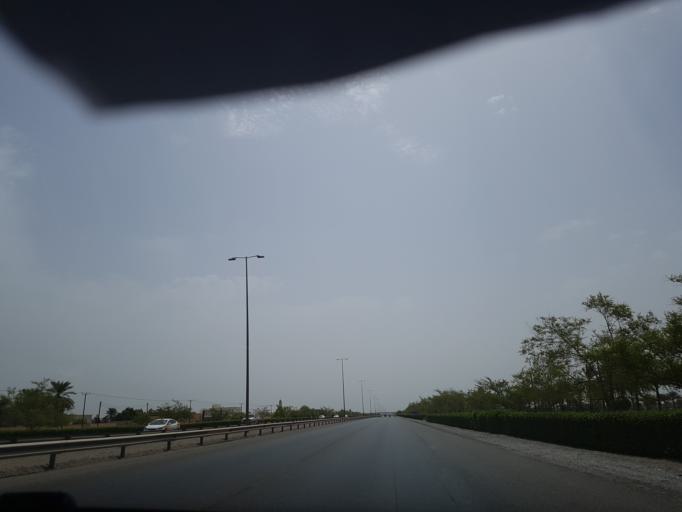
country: OM
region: Al Batinah
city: Barka'
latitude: 23.7310
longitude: 57.6987
